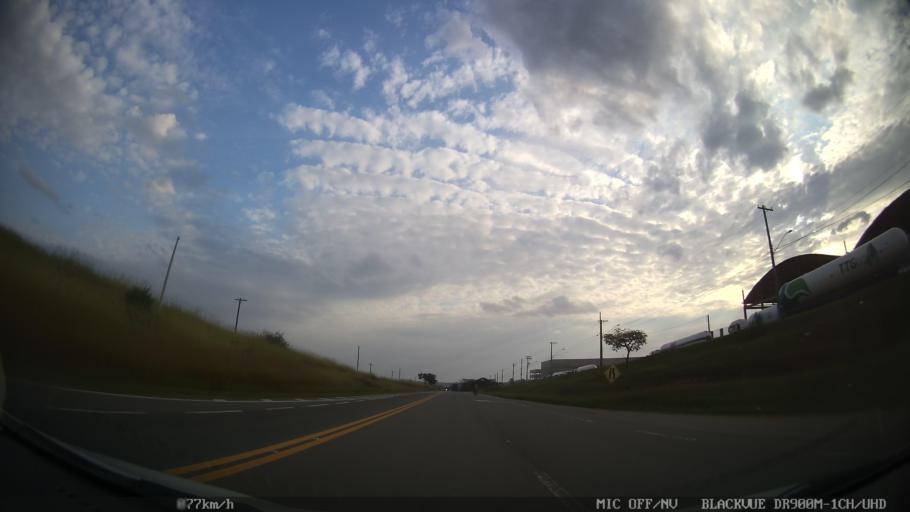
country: BR
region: Sao Paulo
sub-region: Americana
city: Americana
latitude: -22.6364
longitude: -47.3185
